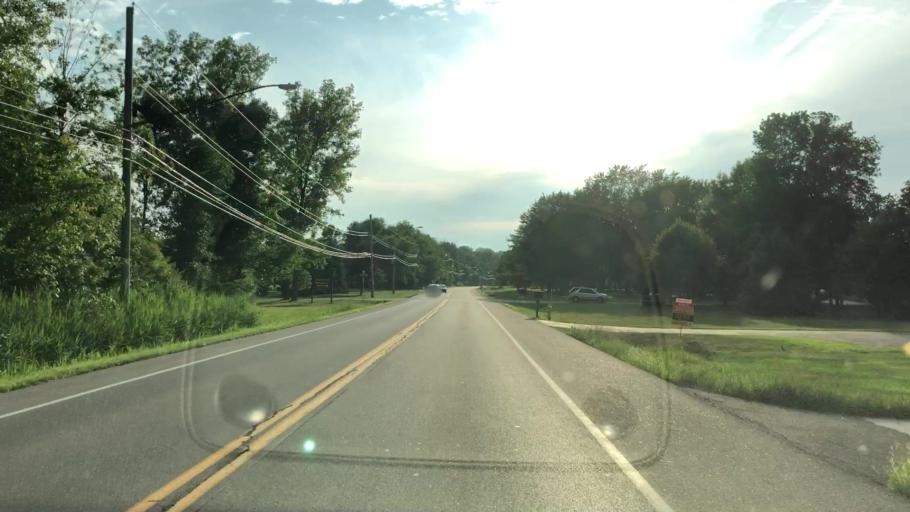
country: US
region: New York
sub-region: Erie County
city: Depew
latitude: 42.8925
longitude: -78.7174
